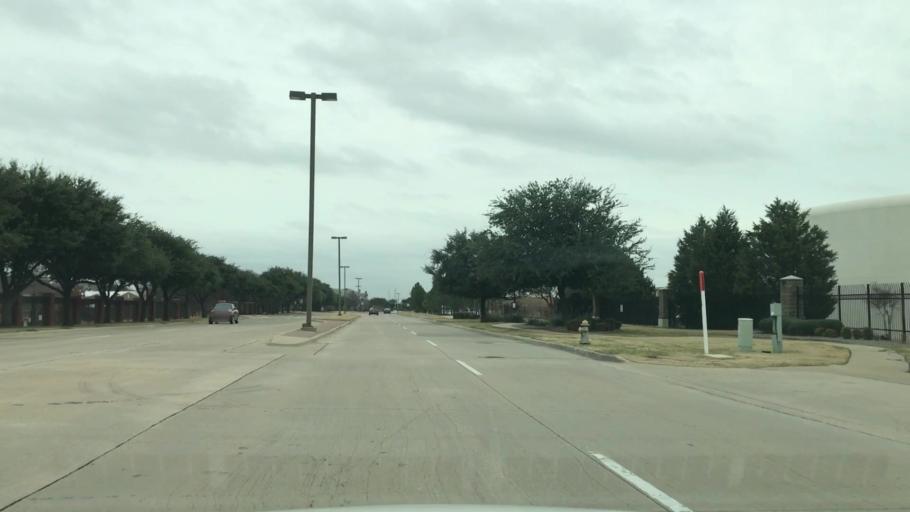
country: US
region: Texas
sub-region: Dallas County
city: Coppell
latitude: 32.9218
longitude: -96.9637
